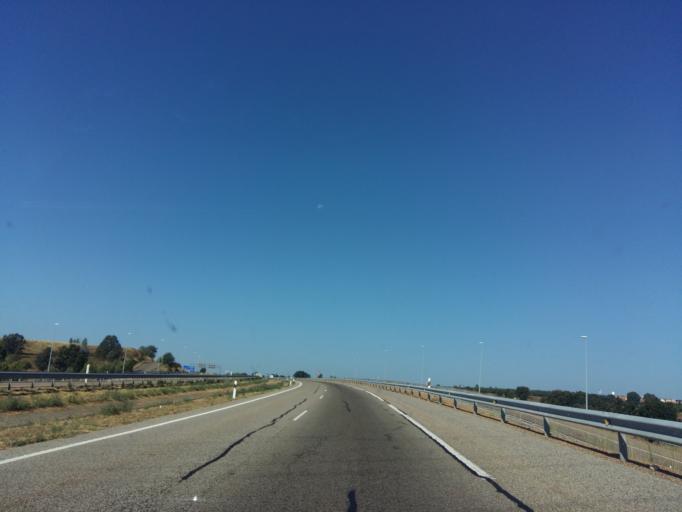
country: ES
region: Castille and Leon
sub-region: Provincia de Leon
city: San Andres del Rabanedo
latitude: 42.5765
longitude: -5.6231
